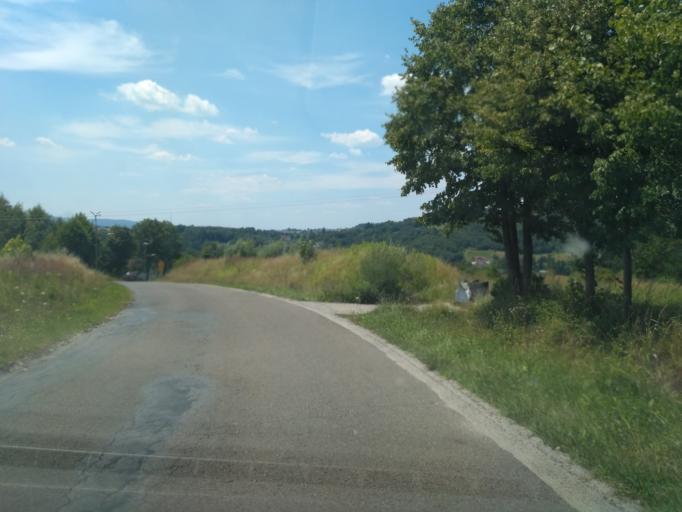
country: PL
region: Subcarpathian Voivodeship
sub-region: Powiat strzyzowski
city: Strzyzow
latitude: 49.8737
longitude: 21.8262
